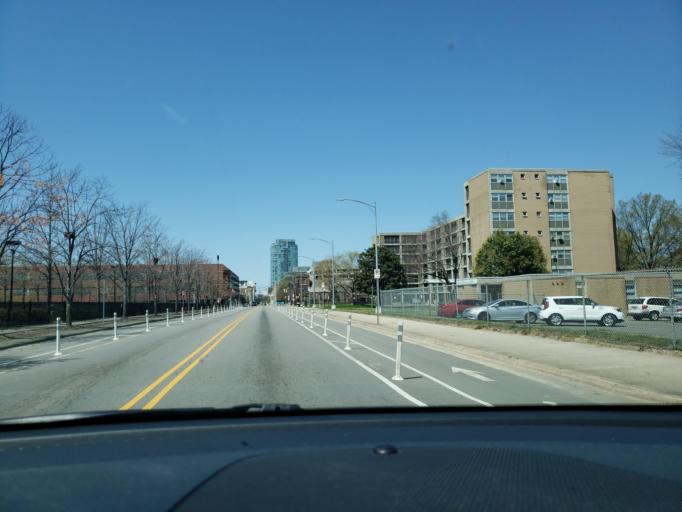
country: US
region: North Carolina
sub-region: Durham County
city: Durham
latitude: 35.9912
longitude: -78.8940
